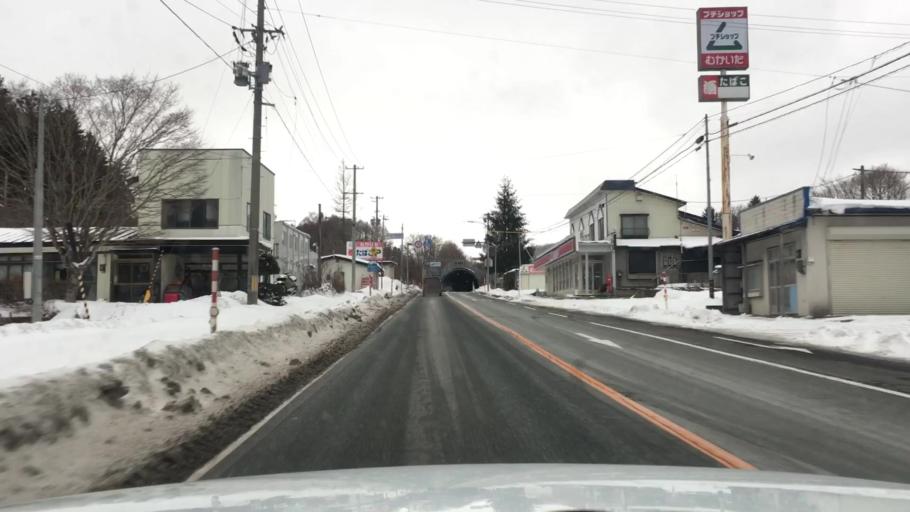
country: JP
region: Iwate
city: Morioka-shi
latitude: 39.6514
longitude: 141.3527
